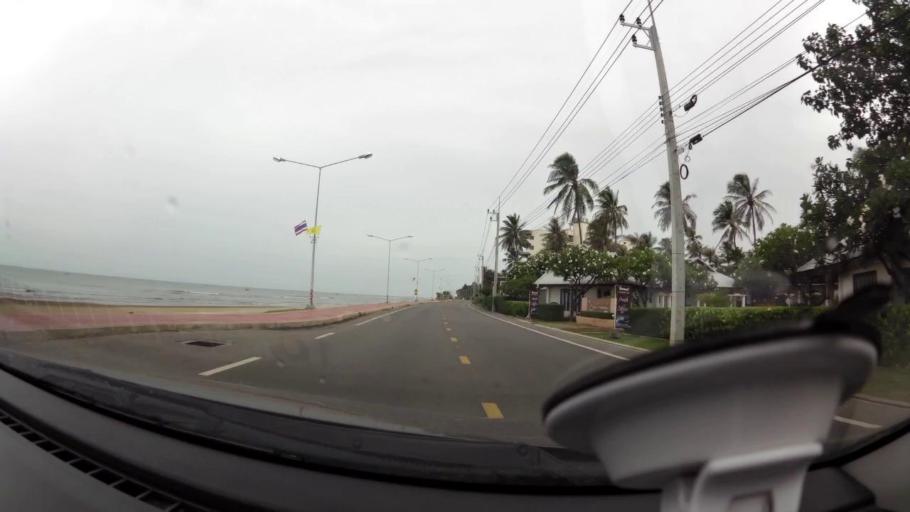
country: TH
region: Prachuap Khiri Khan
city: Pran Buri
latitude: 12.3930
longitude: 99.9966
